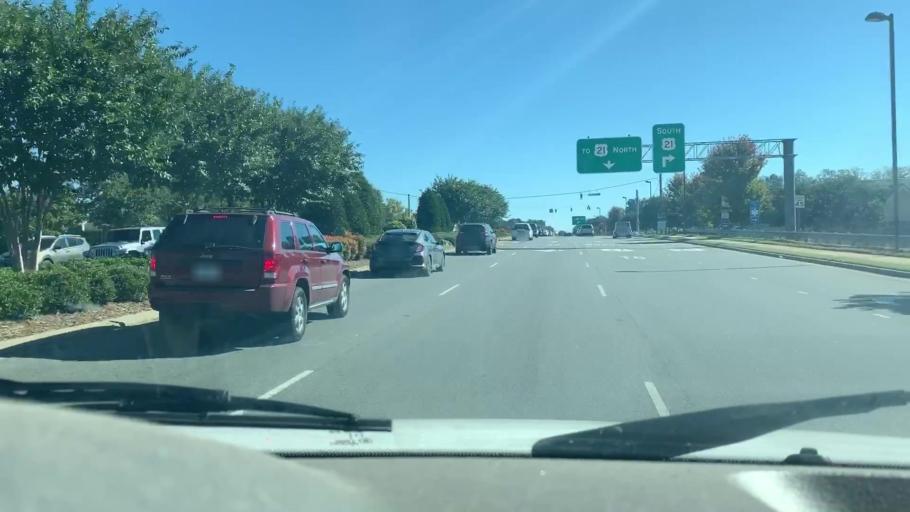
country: US
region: North Carolina
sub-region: Mecklenburg County
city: Huntersville
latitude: 35.4423
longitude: -80.8673
